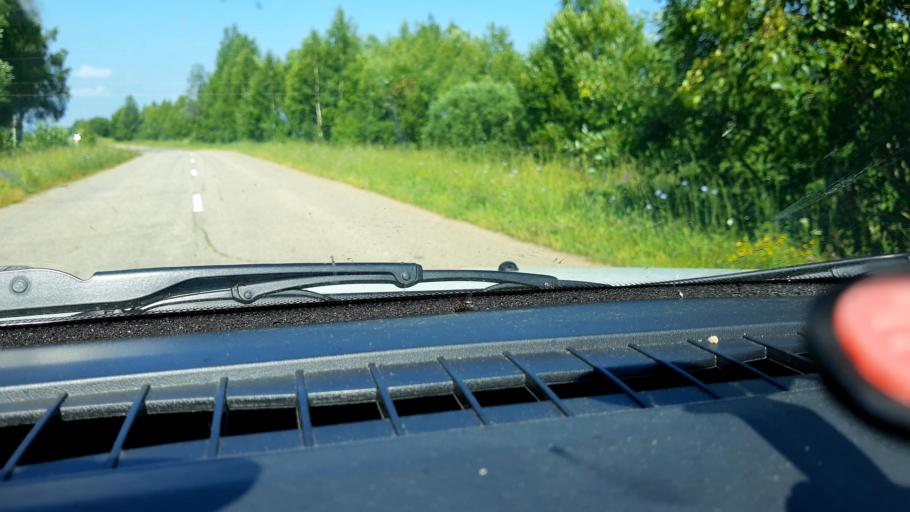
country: RU
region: Nizjnij Novgorod
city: Sharanga
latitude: 57.0096
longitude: 46.6902
